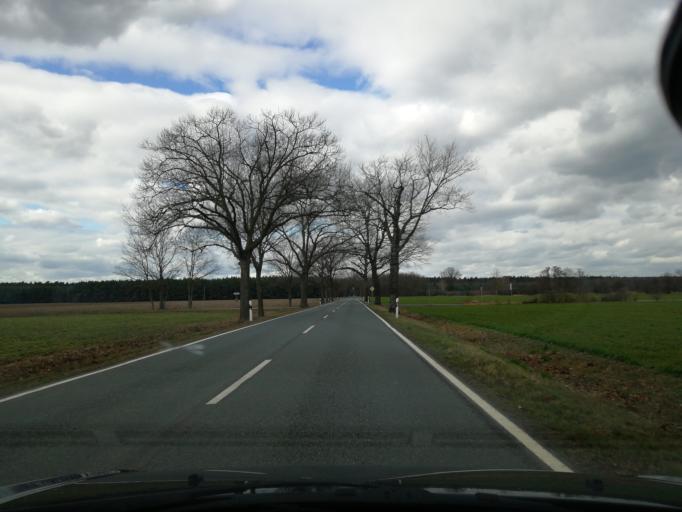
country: DE
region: Brandenburg
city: Altdobern
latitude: 51.6928
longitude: 14.0939
